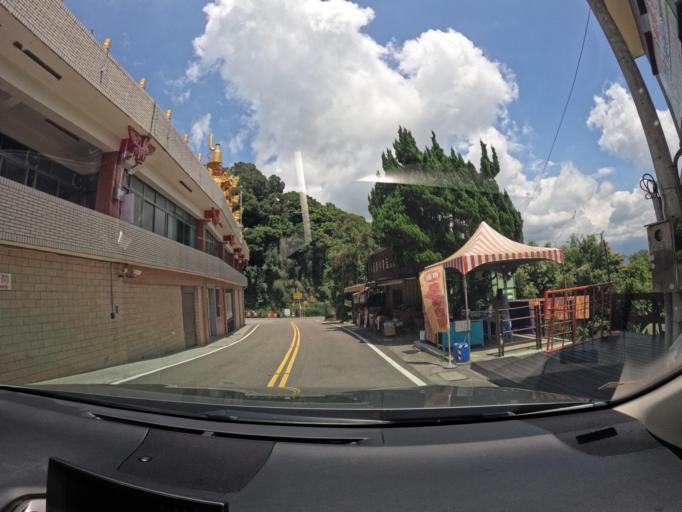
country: TW
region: Taiwan
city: Fengyuan
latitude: 24.3876
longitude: 120.8255
